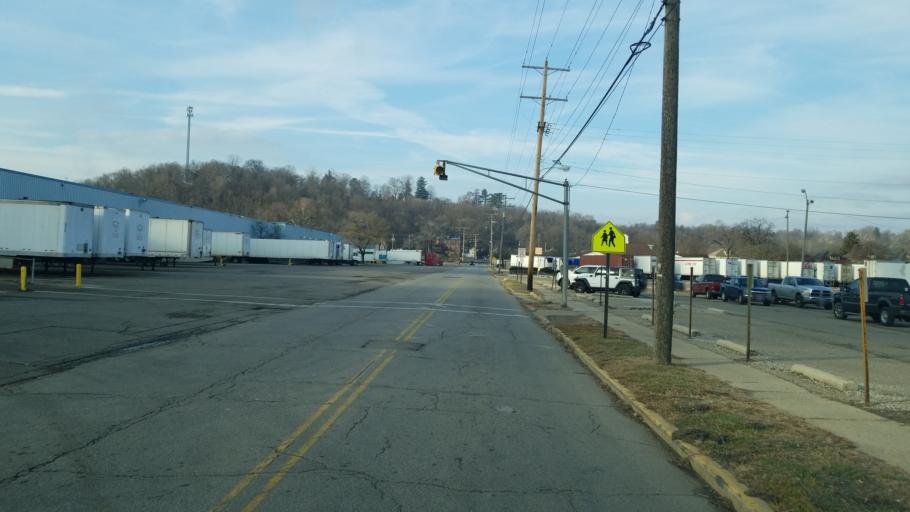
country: US
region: Ohio
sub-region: Ross County
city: Chillicothe
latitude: 39.3264
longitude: -82.9760
